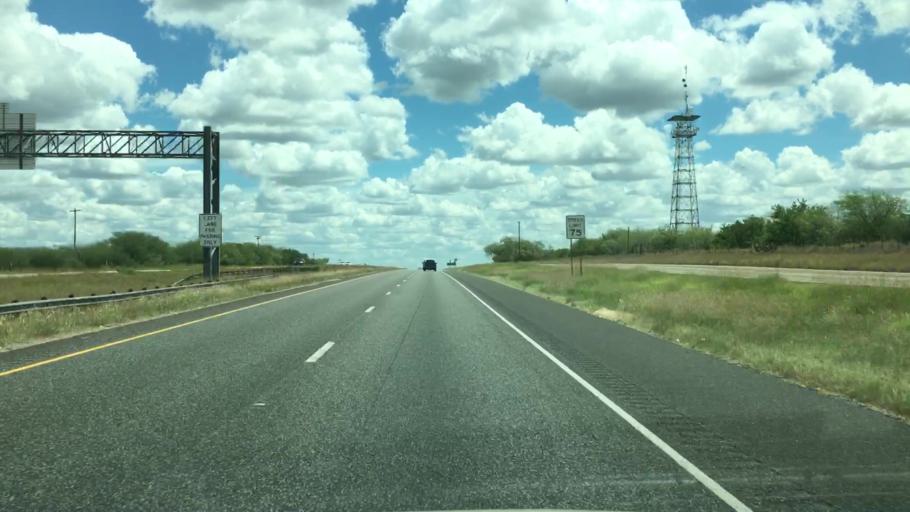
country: US
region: Texas
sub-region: Atascosa County
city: Pleasanton
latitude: 28.9021
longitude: -98.4237
